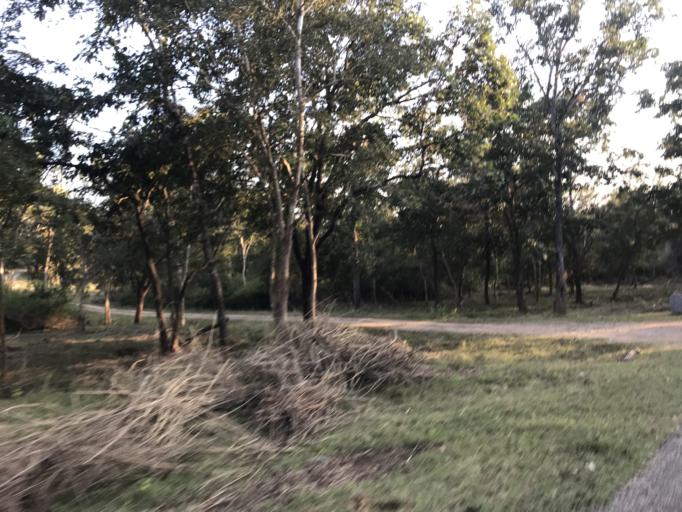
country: IN
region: Karnataka
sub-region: Mysore
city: Heggadadevankote
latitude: 12.0003
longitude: 76.2436
